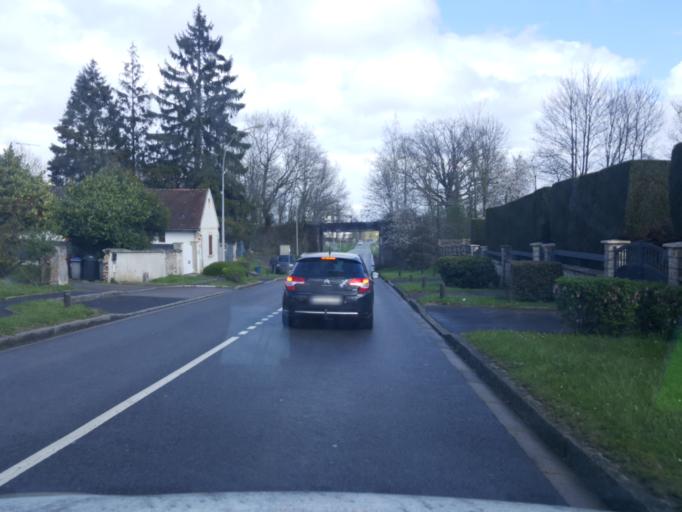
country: FR
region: Picardie
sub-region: Departement de l'Oise
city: Auneuil
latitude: 49.3767
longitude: 1.9921
